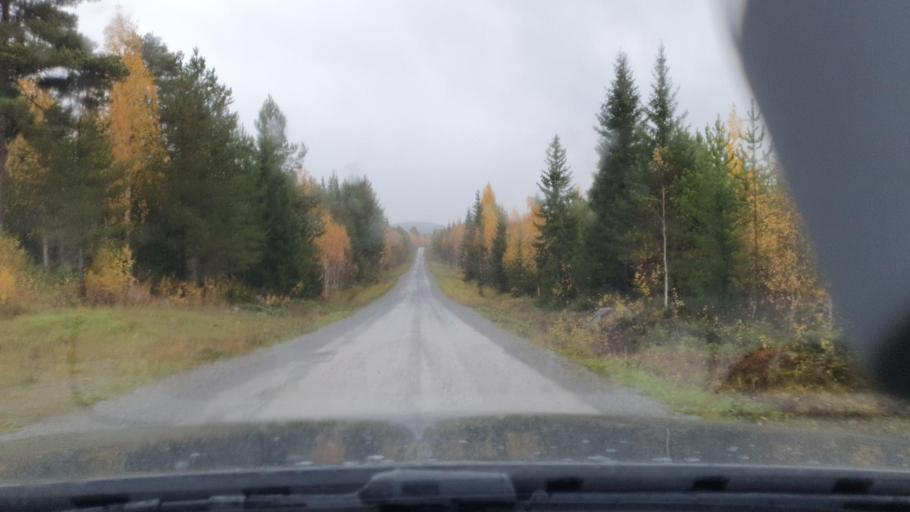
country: SE
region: Jaemtland
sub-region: Stroemsunds Kommun
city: Stroemsund
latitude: 63.5417
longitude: 15.5775
